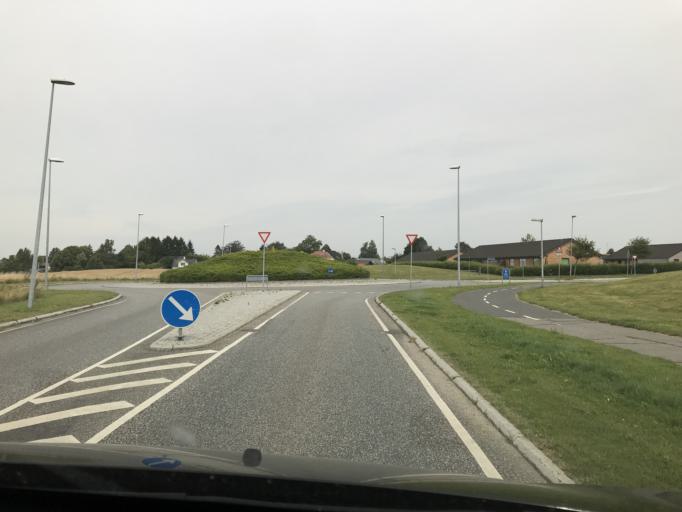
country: DK
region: South Denmark
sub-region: Assens Kommune
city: Arup
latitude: 55.3686
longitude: 10.0464
